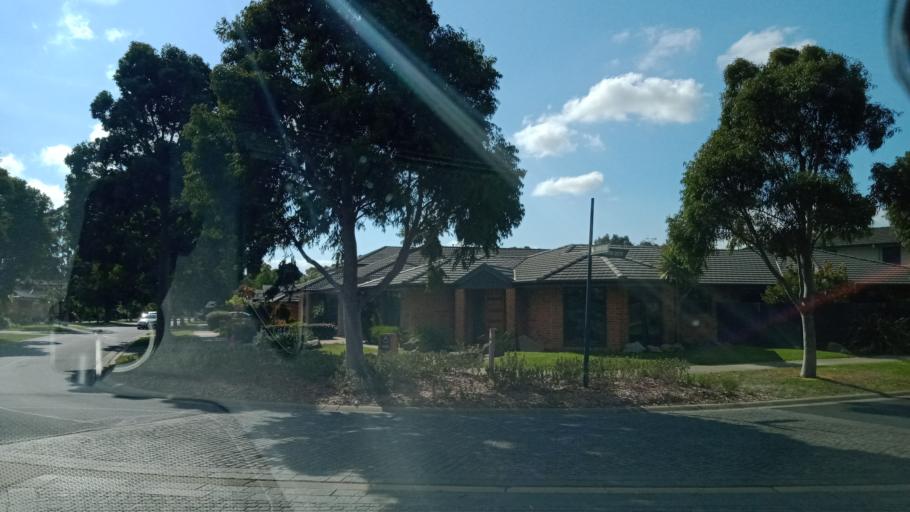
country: AU
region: Victoria
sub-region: Frankston
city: Sandhurst
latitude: -38.0825
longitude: 145.2057
